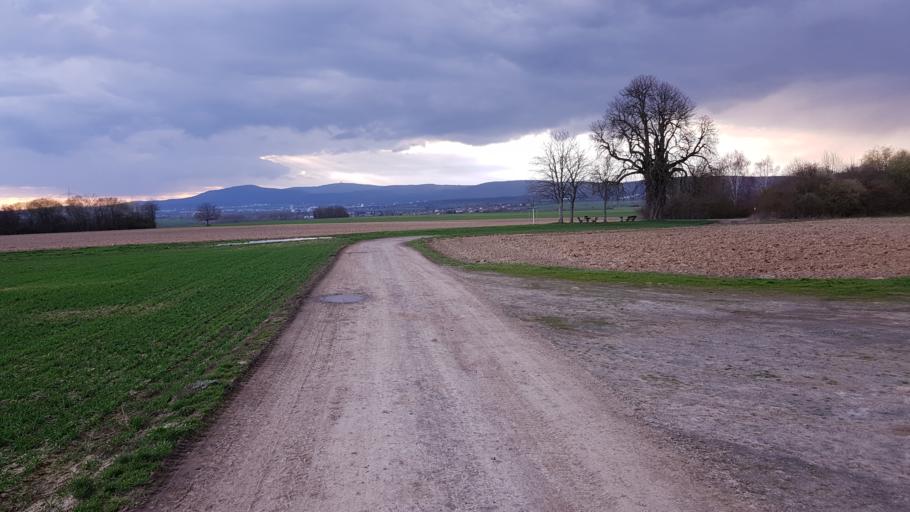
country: DE
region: Hesse
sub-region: Regierungsbezirk Darmstadt
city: Bad Vilbel
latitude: 50.2213
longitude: 8.7230
